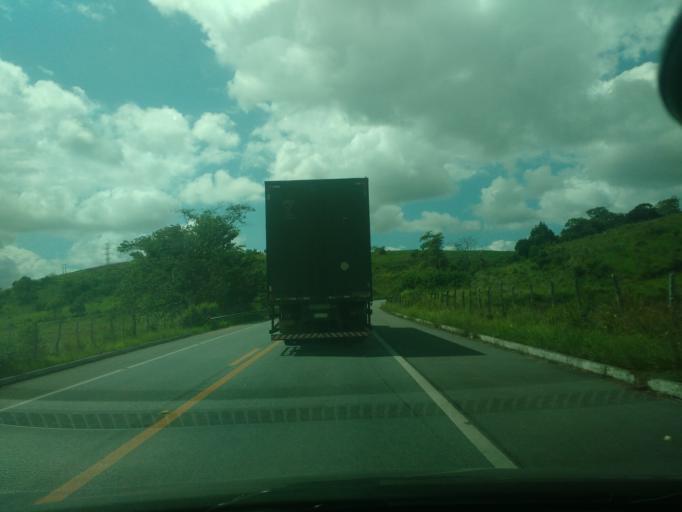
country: BR
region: Alagoas
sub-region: Messias
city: Messias
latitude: -9.3474
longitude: -35.8777
